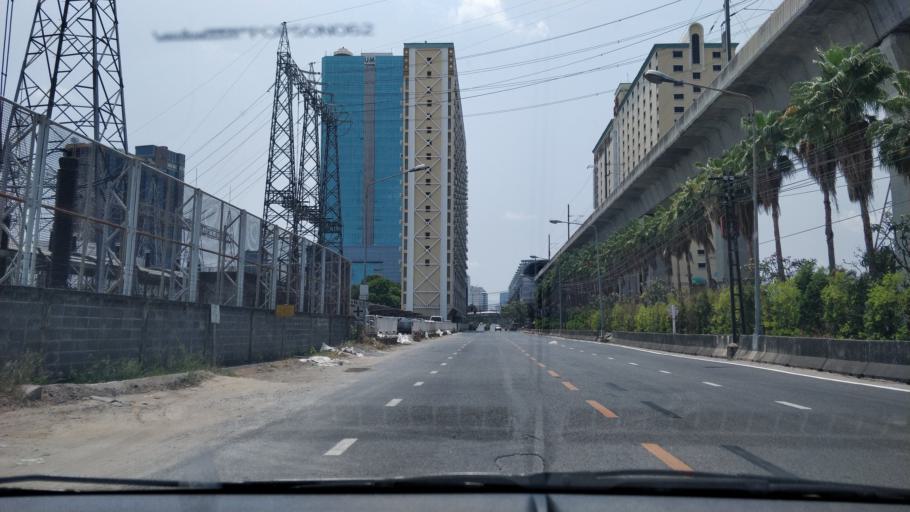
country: TH
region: Bangkok
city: Watthana
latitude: 13.7424
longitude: 100.6037
